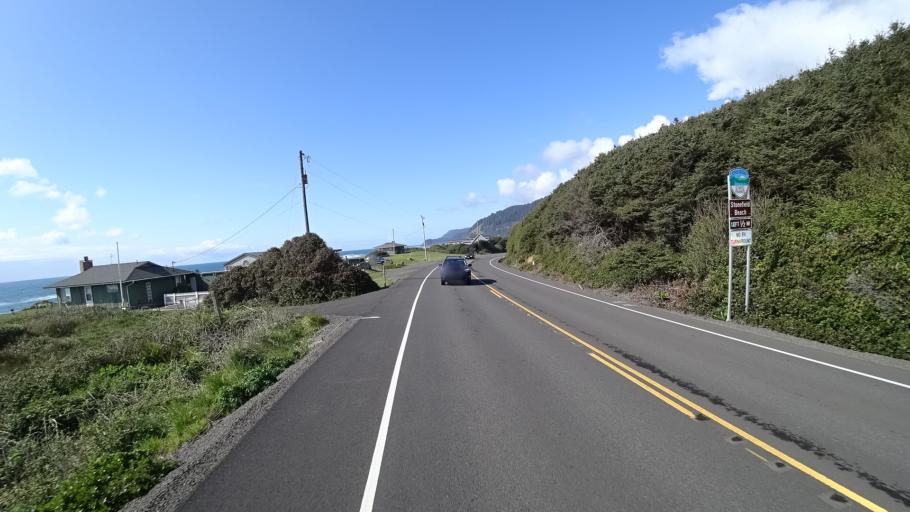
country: US
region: Oregon
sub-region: Lincoln County
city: Waldport
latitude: 44.2176
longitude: -124.1136
